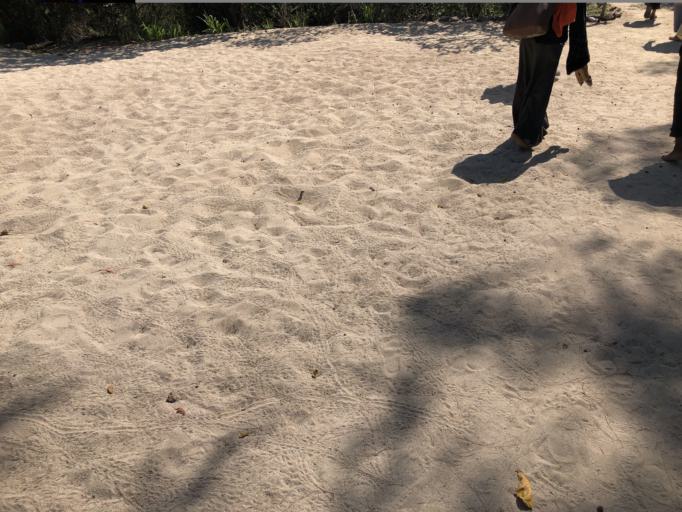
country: TZ
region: Zanzibar Urban/West
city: Zanzibar
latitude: -6.2807
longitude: 39.1766
